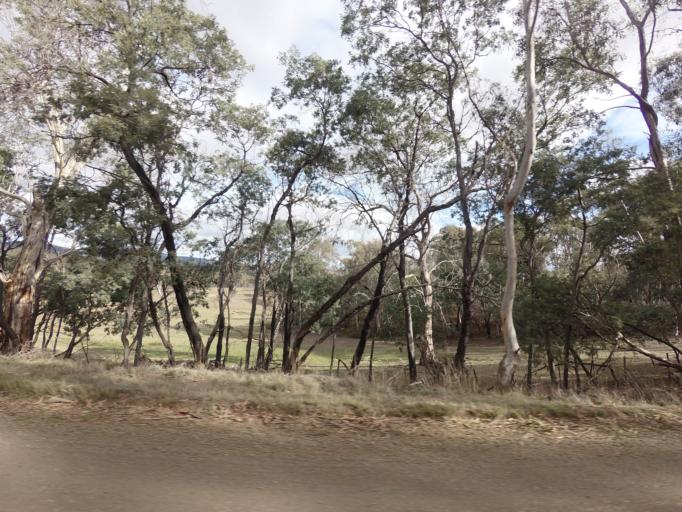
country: AU
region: Tasmania
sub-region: Brighton
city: Bridgewater
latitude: -42.4612
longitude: 147.2653
